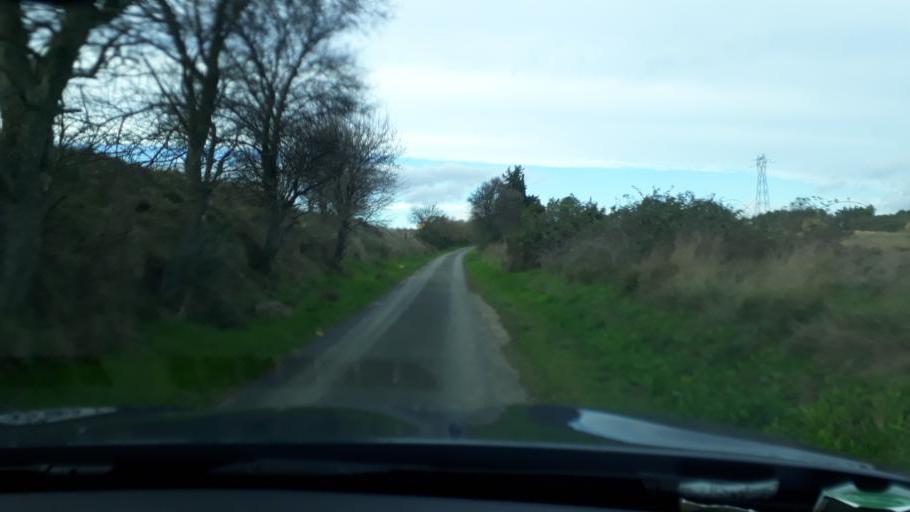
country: FR
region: Languedoc-Roussillon
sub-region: Departement de l'Herault
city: Florensac
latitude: 43.4094
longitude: 3.4593
